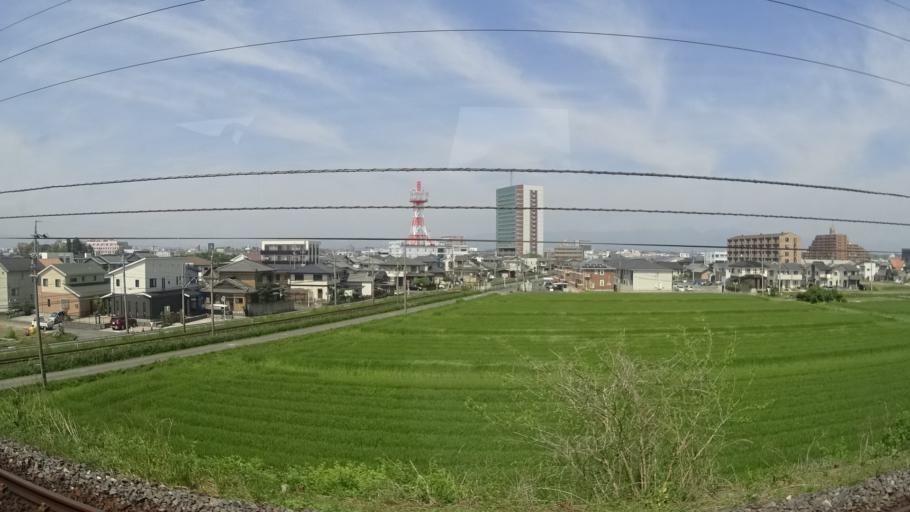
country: JP
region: Mie
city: Suzuka
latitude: 34.8796
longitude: 136.5894
